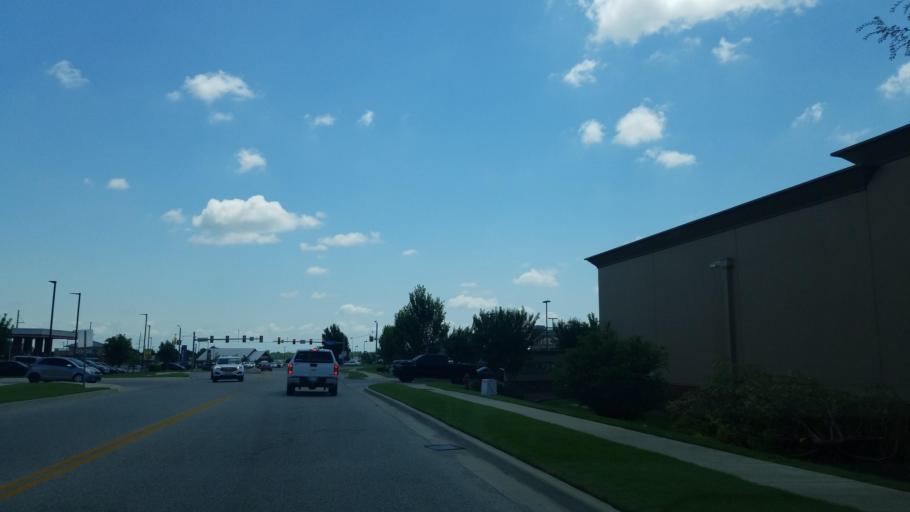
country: US
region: Oklahoma
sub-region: Tulsa County
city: Broken Arrow
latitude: 36.0675
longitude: -95.7814
